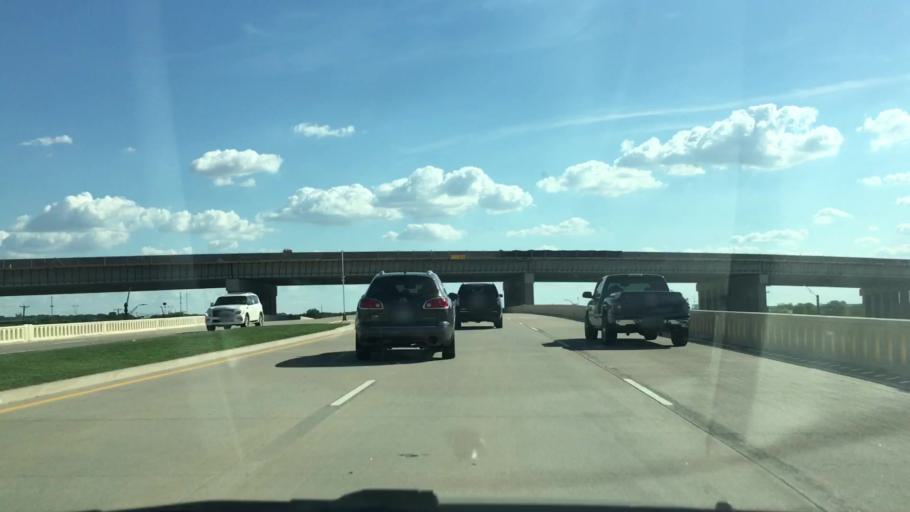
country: US
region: Texas
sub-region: Collin County
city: Prosper
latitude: 33.2208
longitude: -96.7997
